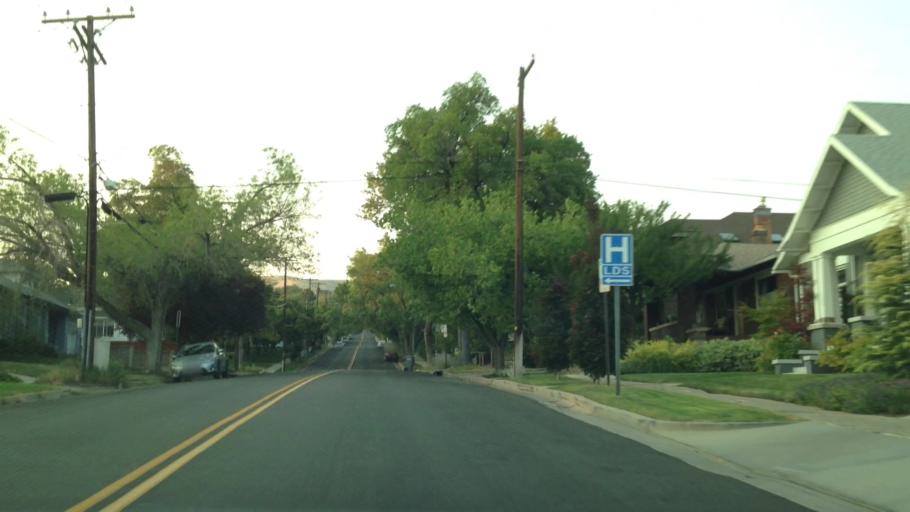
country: US
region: Utah
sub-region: Salt Lake County
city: Salt Lake City
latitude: 40.7776
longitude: -111.8775
